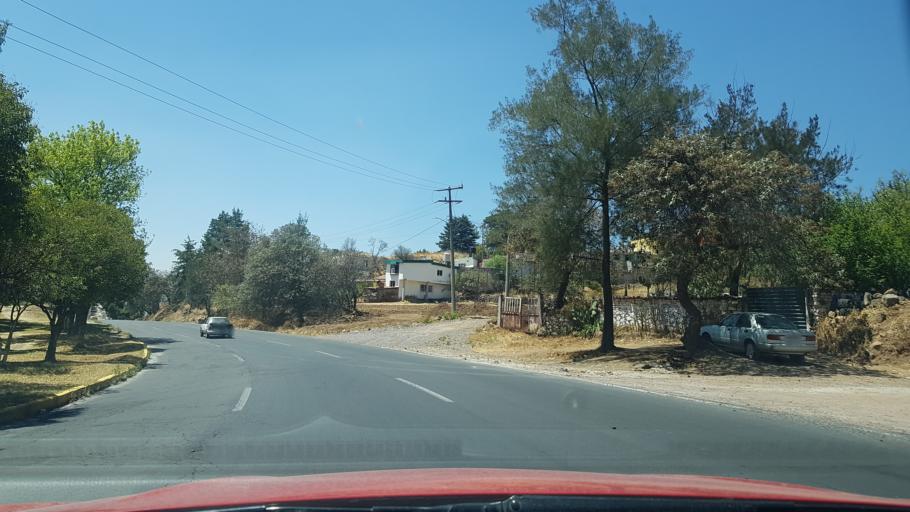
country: MX
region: Mexico
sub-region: Atlacomulco
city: Santa Cruz Bombatevi
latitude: 19.8037
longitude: -99.8847
